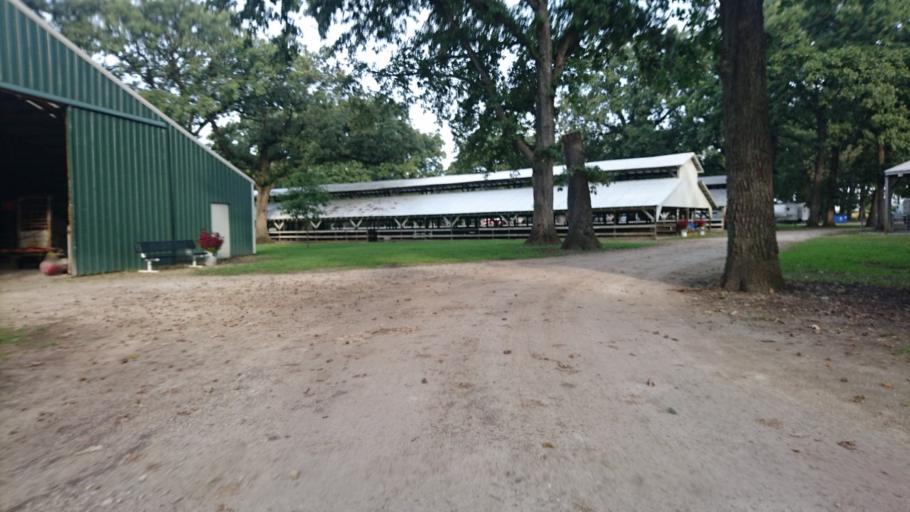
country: US
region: Illinois
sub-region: Livingston County
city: Pontiac
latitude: 40.8922
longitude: -88.6649
